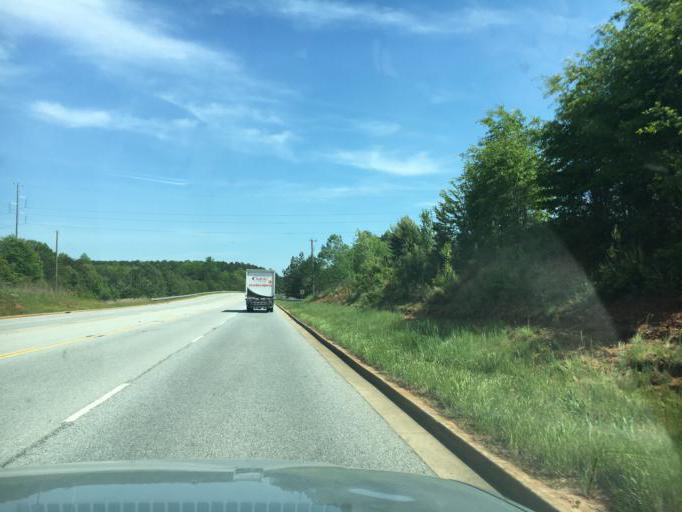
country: US
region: South Carolina
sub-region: Cherokee County
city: Blacksburg
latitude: 35.1301
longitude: -81.5073
